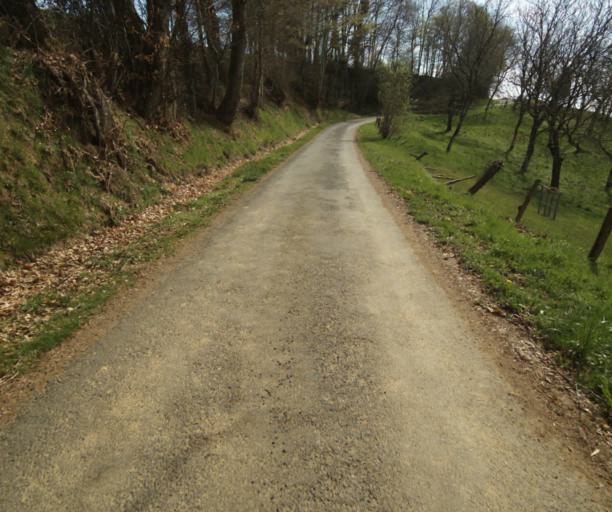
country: FR
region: Limousin
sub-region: Departement de la Correze
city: Naves
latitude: 45.3643
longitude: 1.7934
